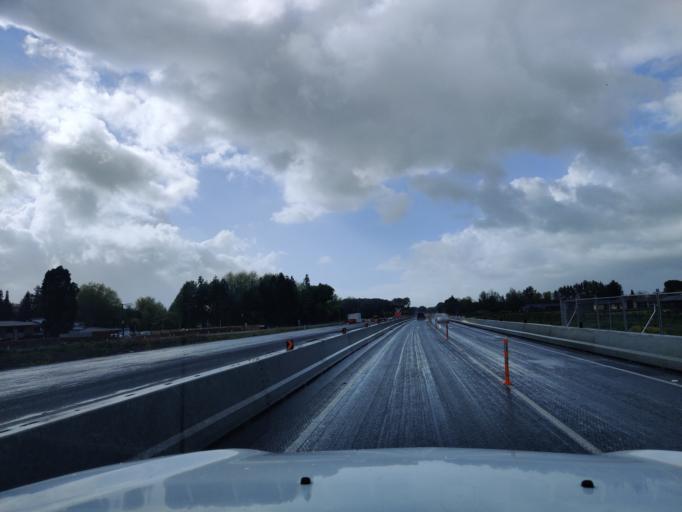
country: NZ
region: Waikato
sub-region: Hamilton City
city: Hamilton
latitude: -37.8203
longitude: 175.3467
